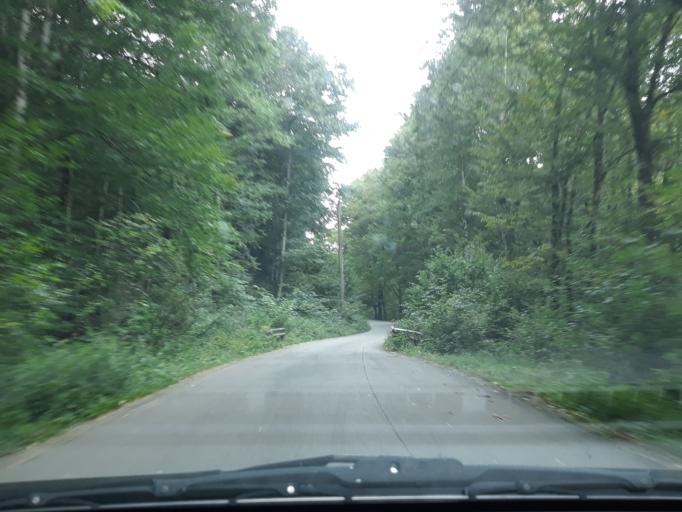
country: RO
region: Bihor
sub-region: Comuna Pietroasa
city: Pietroasa
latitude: 46.5877
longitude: 22.6131
